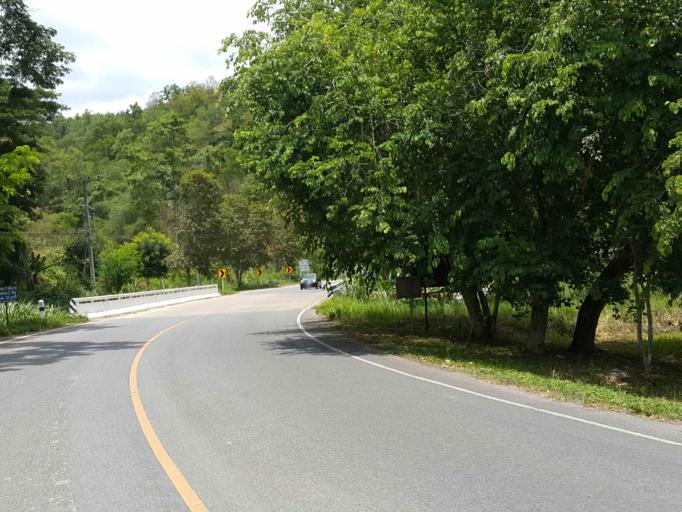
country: TH
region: Chiang Mai
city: Hang Dong
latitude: 18.7641
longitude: 98.8751
